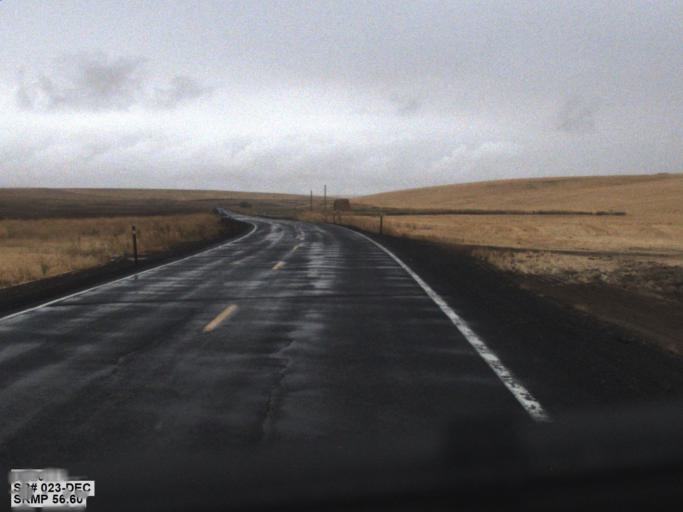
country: US
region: Washington
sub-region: Lincoln County
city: Davenport
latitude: 47.3991
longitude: -118.1608
